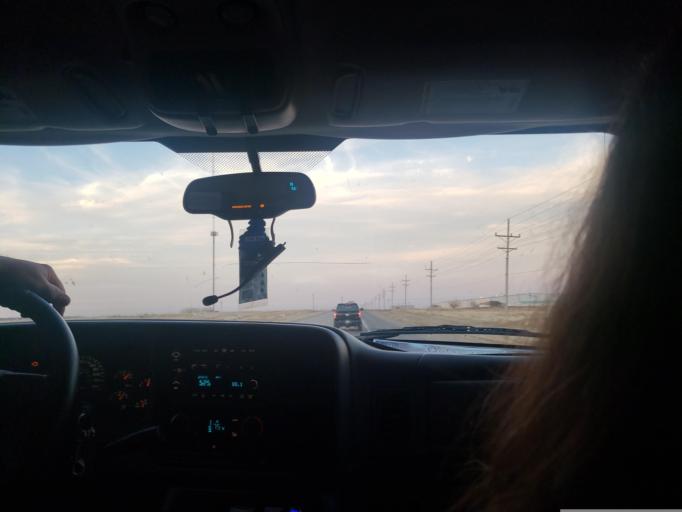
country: US
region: Kansas
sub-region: Seward County
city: Liberal
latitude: 37.0584
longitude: -100.9042
